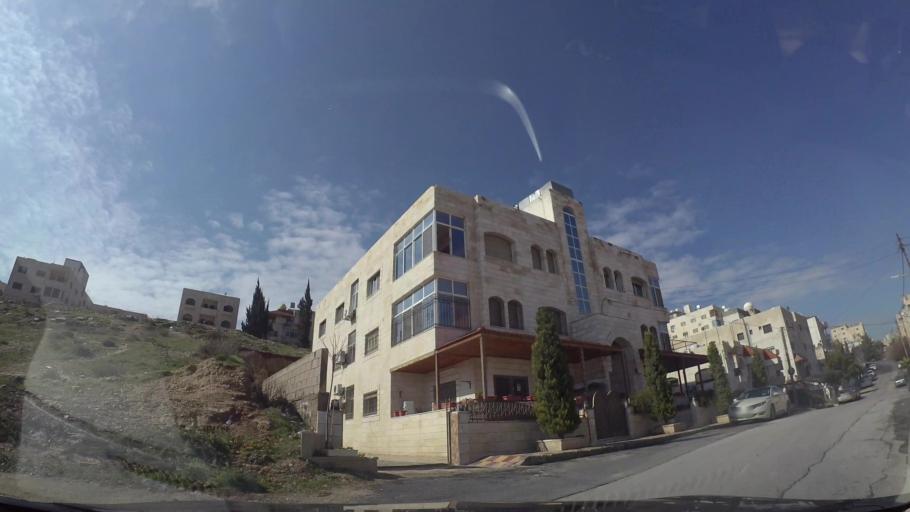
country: JO
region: Amman
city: Al Jubayhah
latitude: 32.0007
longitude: 35.8941
